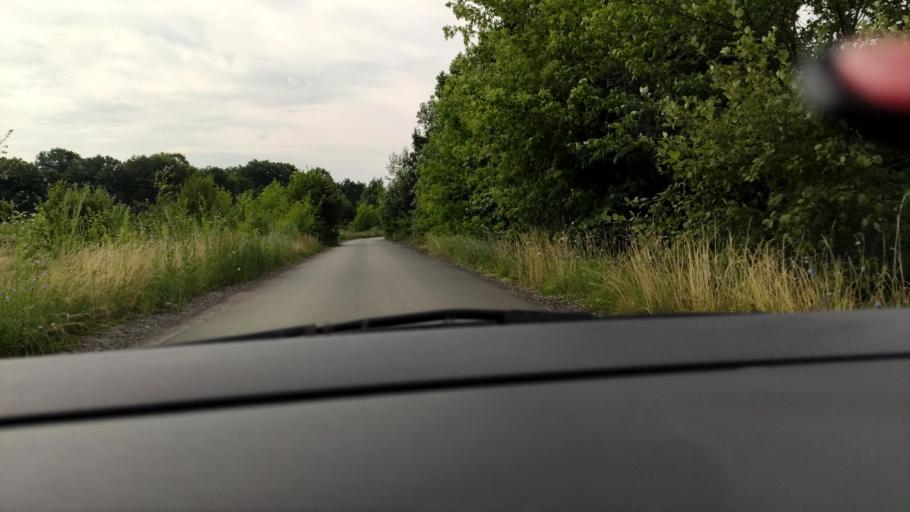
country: RU
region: Voronezj
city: Ramon'
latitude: 51.8969
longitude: 39.3509
